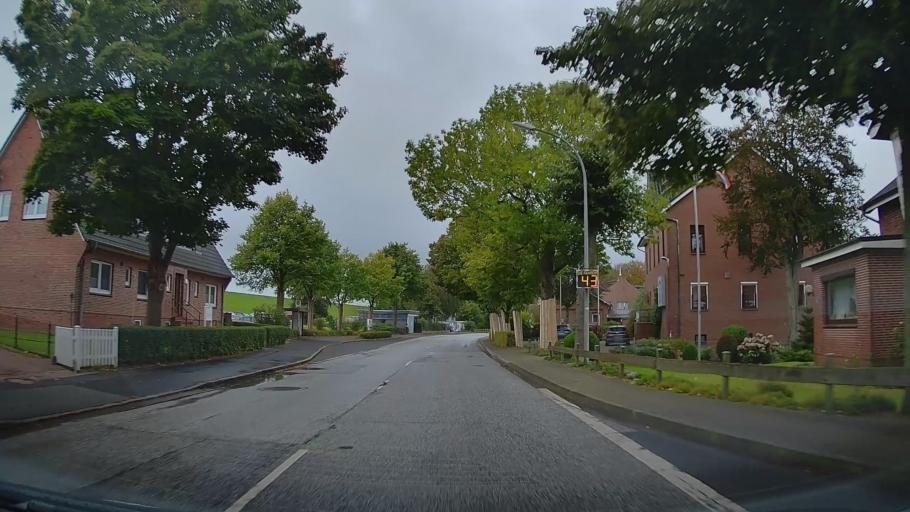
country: DE
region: Schleswig-Holstein
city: Brokdorf
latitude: 53.8622
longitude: 9.3245
